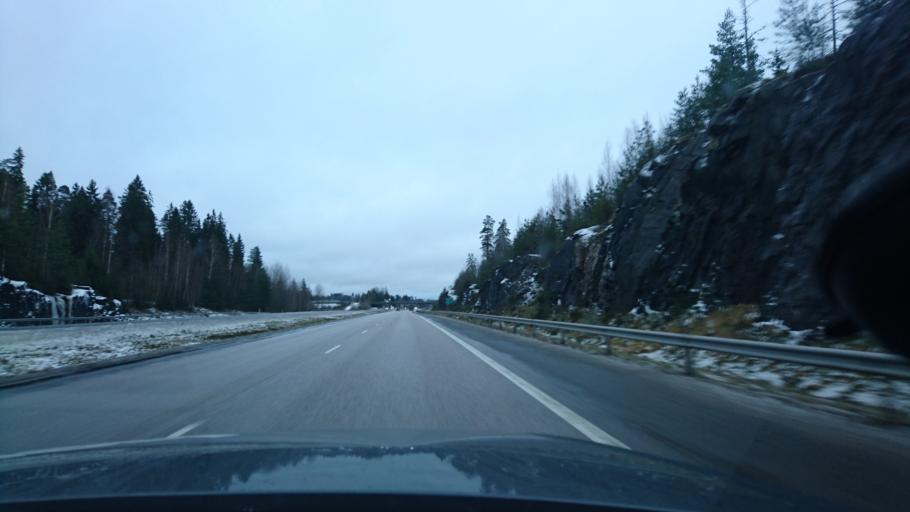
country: FI
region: Uusimaa
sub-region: Helsinki
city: Maentsaelae
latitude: 60.6339
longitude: 25.2944
